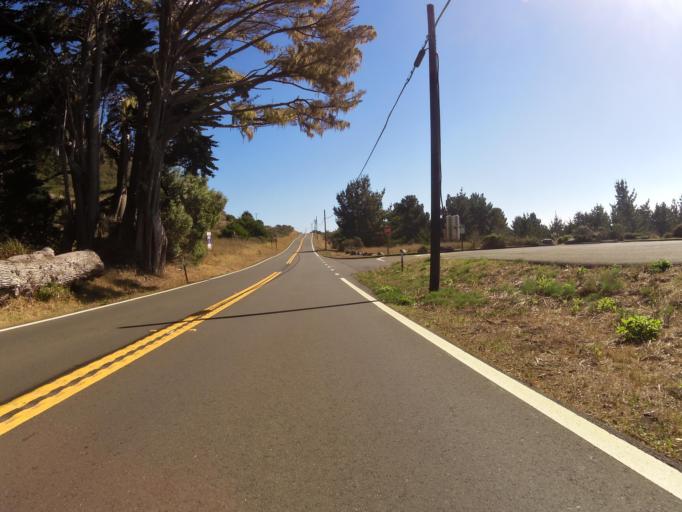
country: US
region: California
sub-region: Mendocino County
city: Fort Bragg
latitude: 39.5994
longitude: -123.7846
